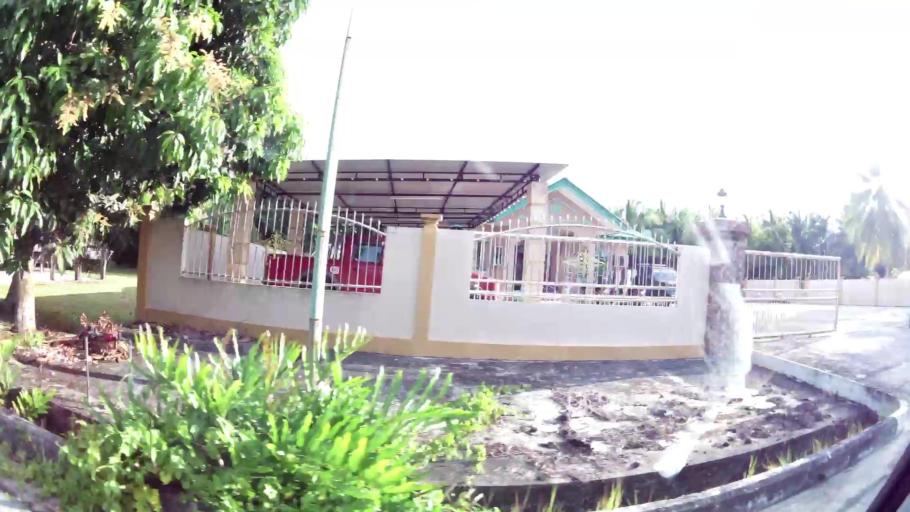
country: BN
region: Brunei and Muara
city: Bandar Seri Begawan
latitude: 4.9517
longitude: 115.0239
